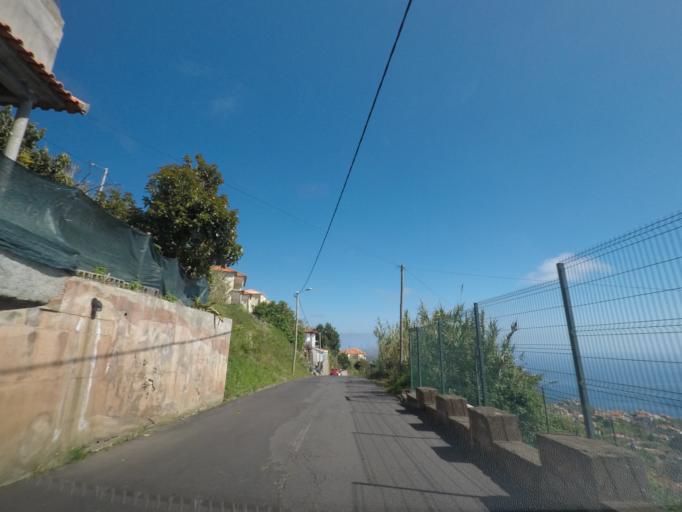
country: PT
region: Madeira
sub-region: Calheta
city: Arco da Calheta
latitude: 32.7048
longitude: -17.1126
